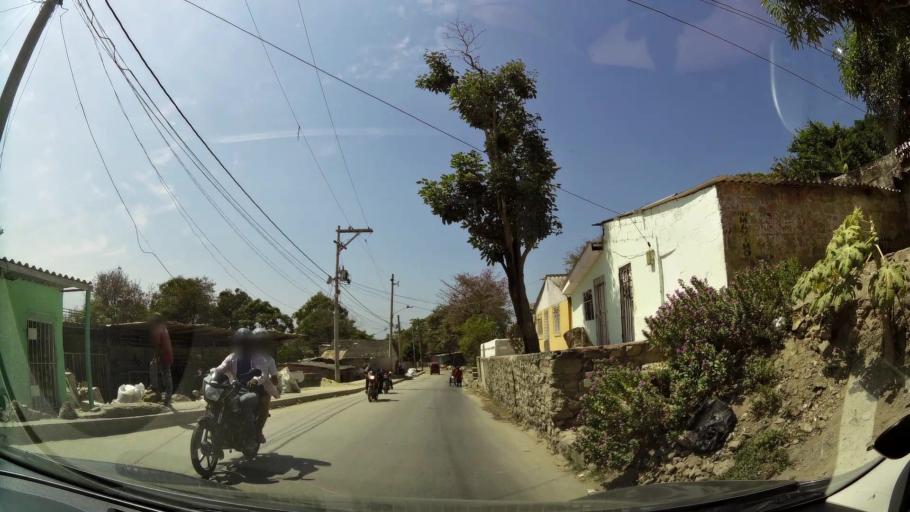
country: CO
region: Atlantico
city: Barranquilla
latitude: 10.9638
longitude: -74.8117
